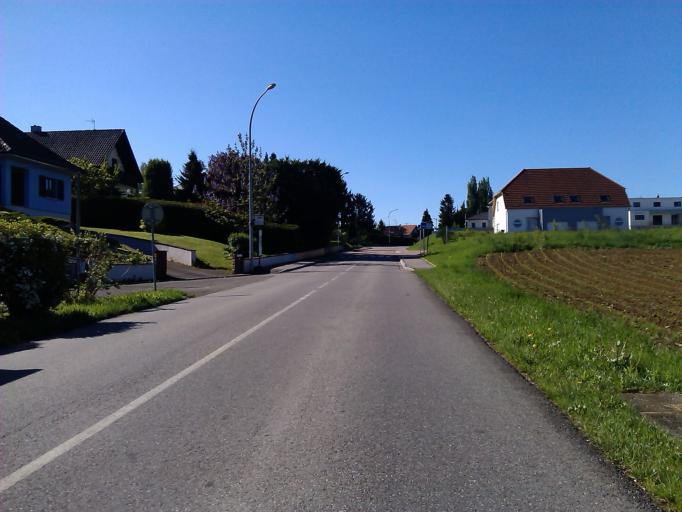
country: FR
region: Alsace
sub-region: Departement du Haut-Rhin
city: Heimsbrunn
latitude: 47.7093
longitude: 7.2254
